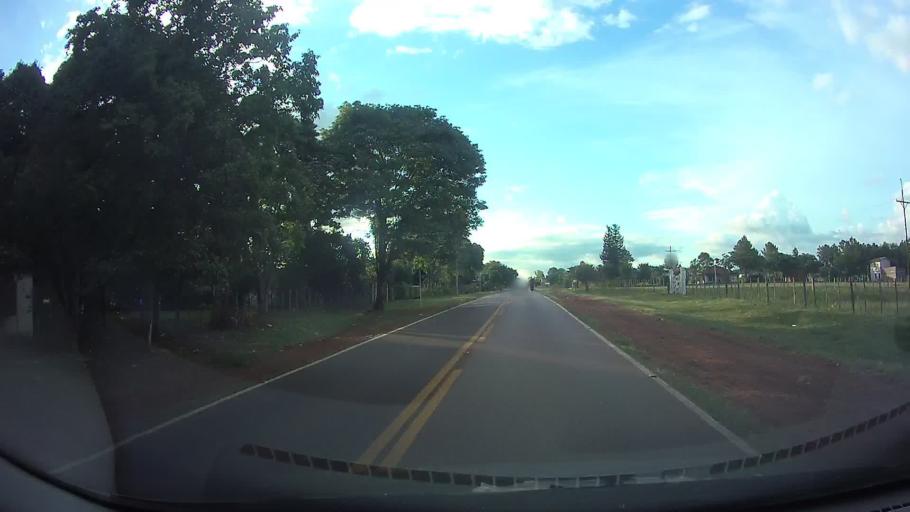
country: PY
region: Paraguari
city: Carapegua
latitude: -25.7986
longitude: -57.1947
